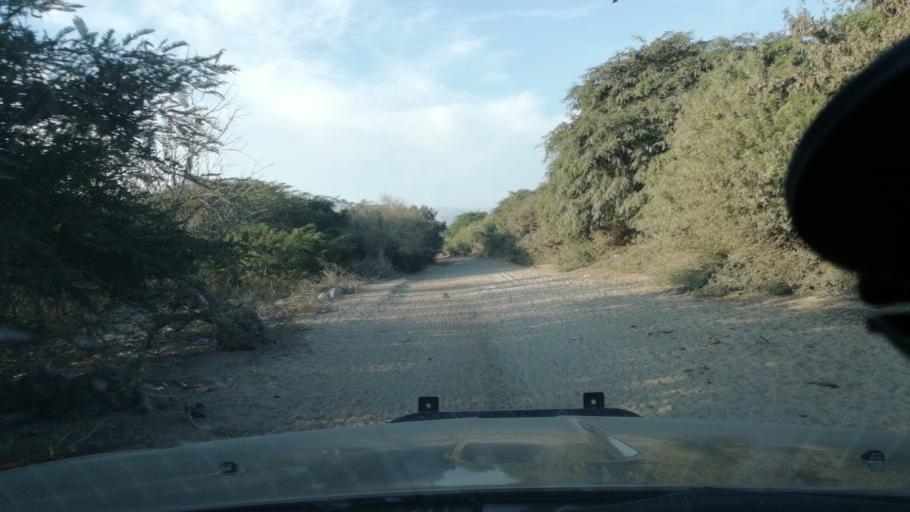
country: PE
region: Ica
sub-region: Provincia de Chincha
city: San Pedro
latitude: -13.3442
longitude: -76.1600
